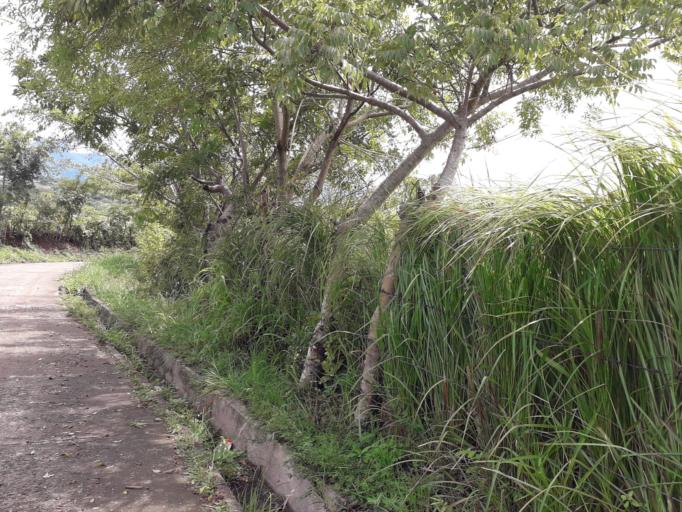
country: GT
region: Santa Rosa
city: Pueblo Nuevo Vinas
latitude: 14.3176
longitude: -90.5578
